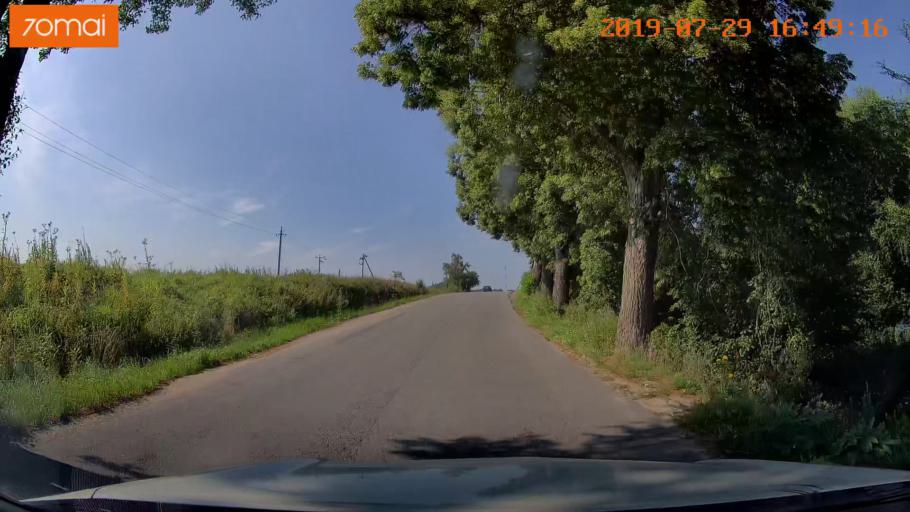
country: RU
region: Kaliningrad
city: Primorsk
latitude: 54.7925
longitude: 20.0667
